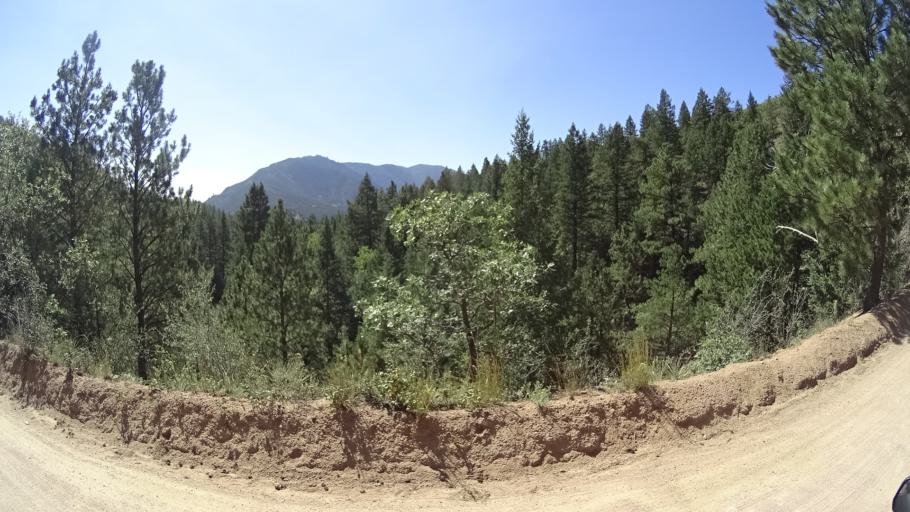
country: US
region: Colorado
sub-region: El Paso County
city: Manitou Springs
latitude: 38.7990
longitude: -104.8840
